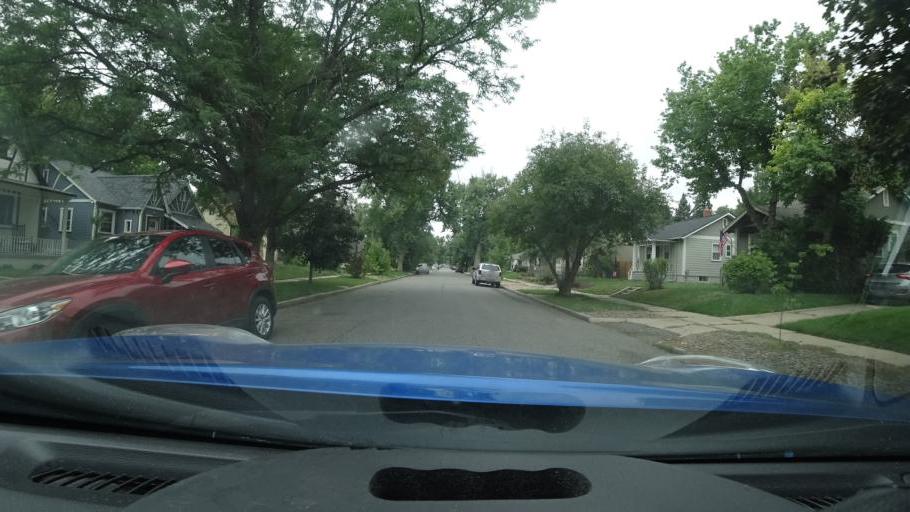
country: US
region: Colorado
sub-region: Arapahoe County
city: Glendale
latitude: 39.6838
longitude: -104.9663
